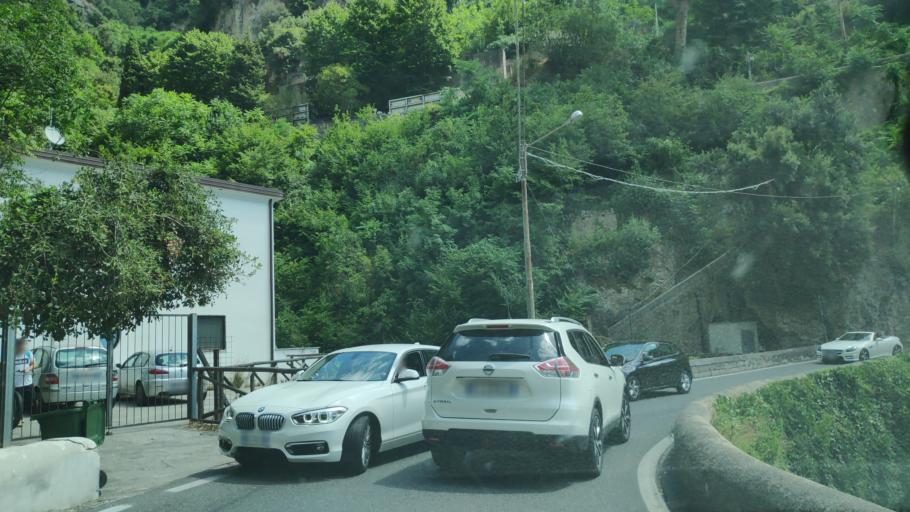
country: IT
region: Campania
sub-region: Provincia di Salerno
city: Conca dei Marini
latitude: 40.6270
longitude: 14.5835
